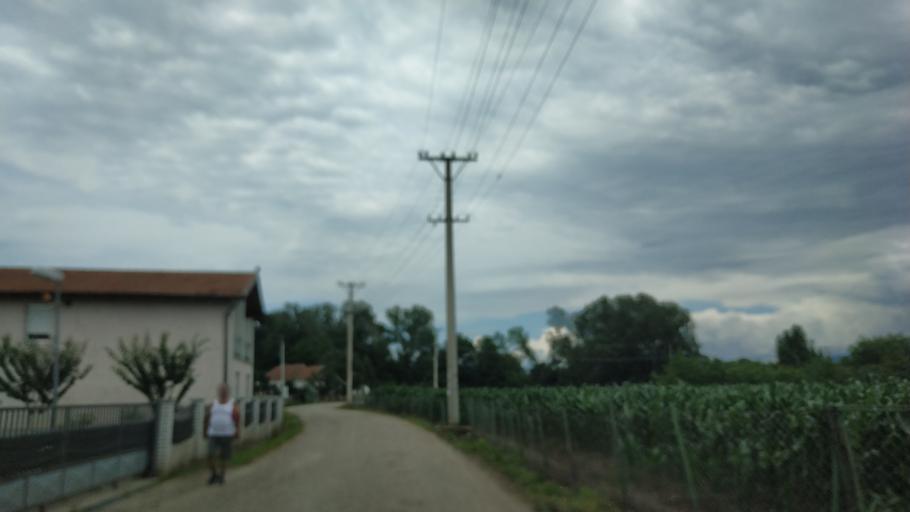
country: RS
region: Central Serbia
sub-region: Nisavski Okrug
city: Razanj
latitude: 43.5914
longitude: 21.6077
